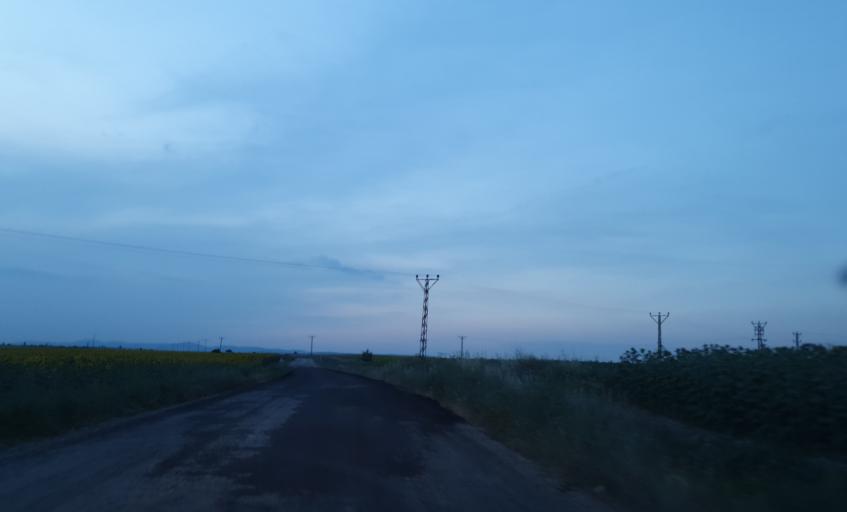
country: TR
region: Kirklareli
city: Vize
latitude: 41.4958
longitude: 27.7519
